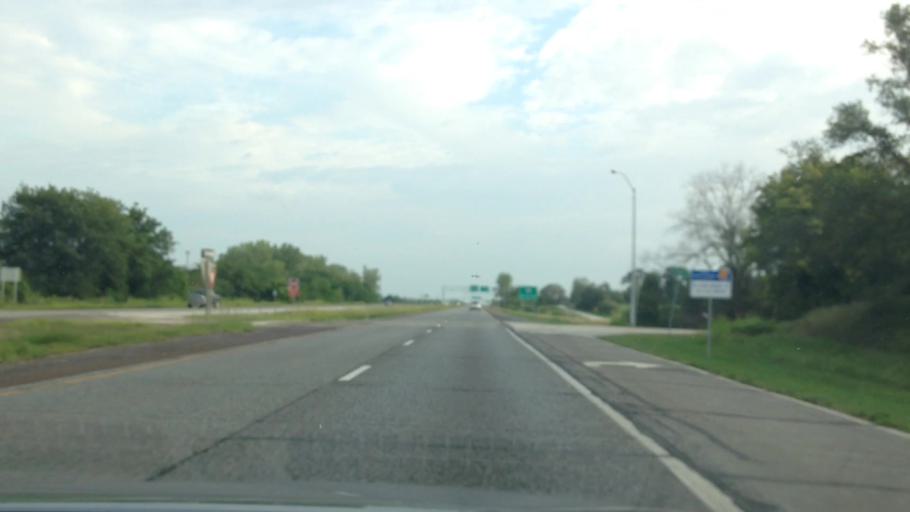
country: US
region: Missouri
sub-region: Clay County
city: Smithville
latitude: 39.3188
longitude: -94.5846
